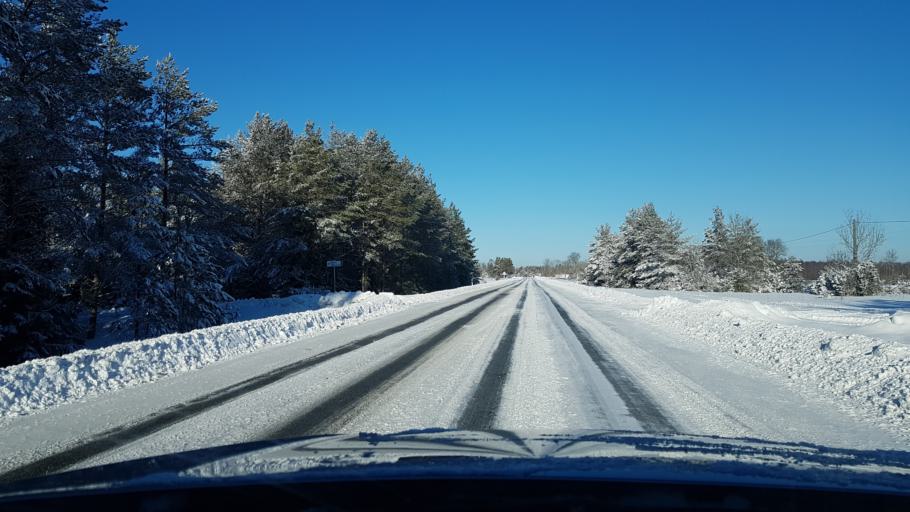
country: EE
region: Hiiumaa
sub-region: Kaerdla linn
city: Kardla
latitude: 58.9509
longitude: 22.7721
